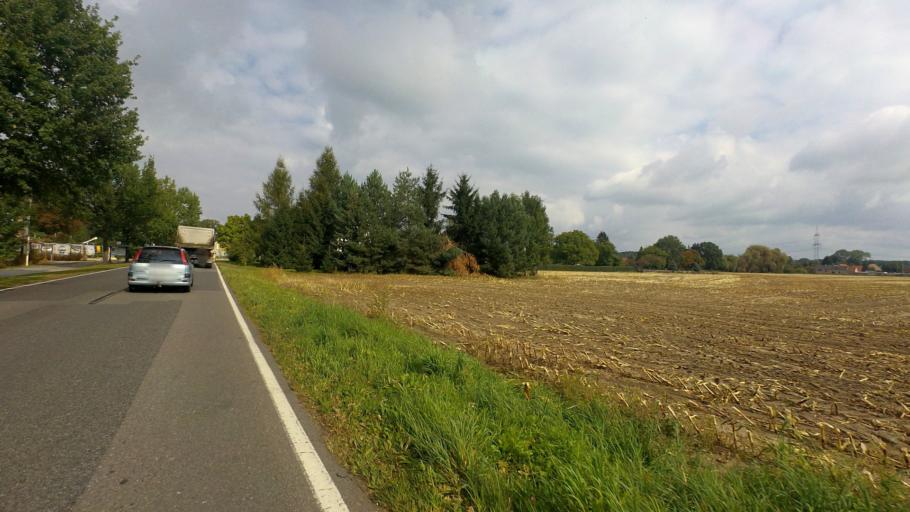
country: DE
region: Brandenburg
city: Bad Liebenwerda
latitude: 51.5353
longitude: 13.4092
